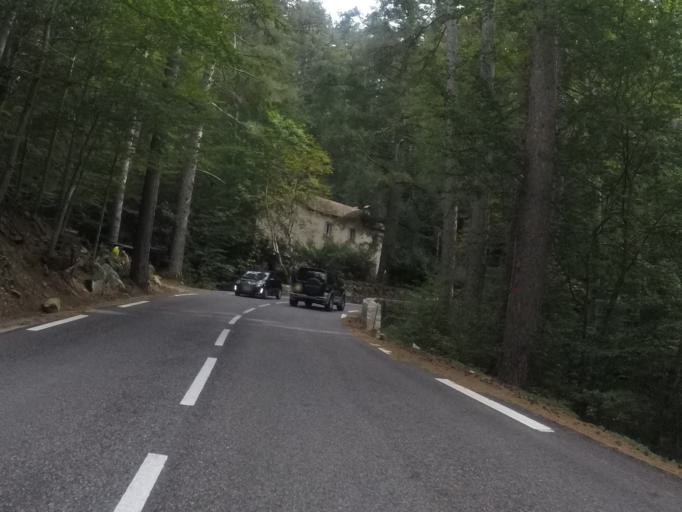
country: FR
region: Corsica
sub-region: Departement de la Haute-Corse
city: Corte
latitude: 42.1248
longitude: 9.1353
